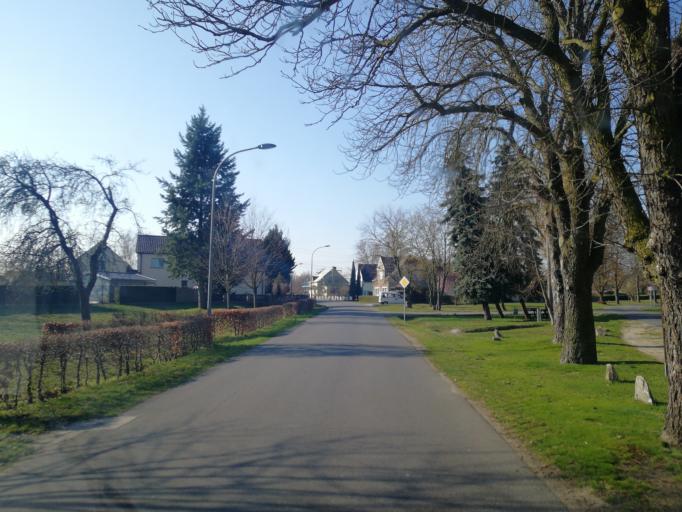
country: DE
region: Brandenburg
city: Drahnsdorf
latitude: 51.8683
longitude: 13.5908
